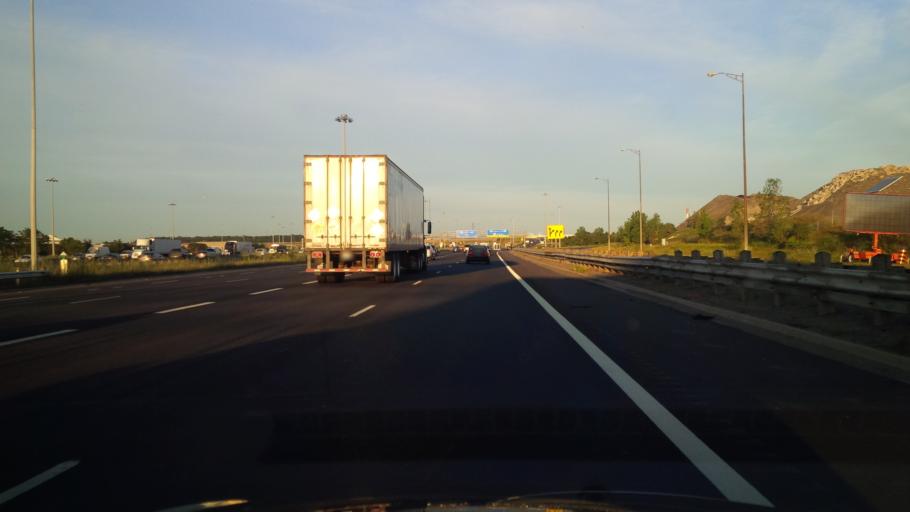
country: CA
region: Ontario
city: Mississauga
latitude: 43.6474
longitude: -79.6411
